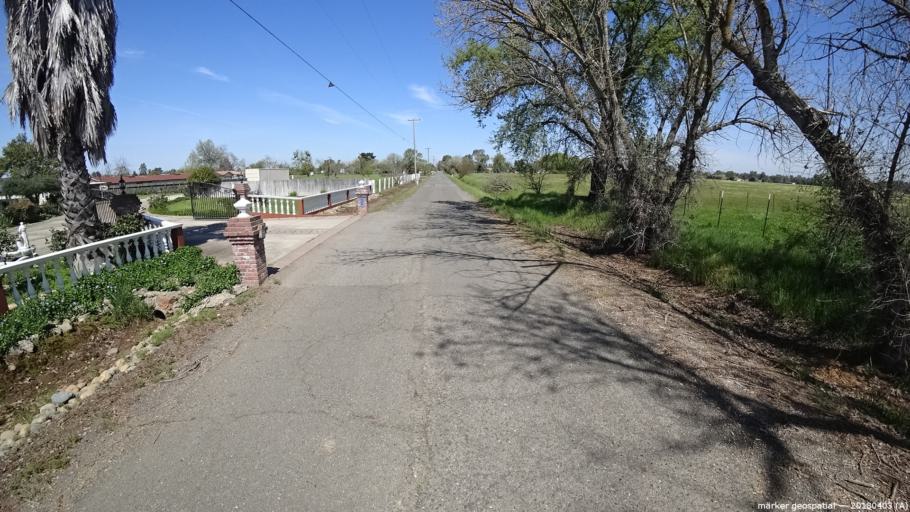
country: US
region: California
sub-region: Sacramento County
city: Wilton
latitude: 38.3965
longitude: -121.2691
